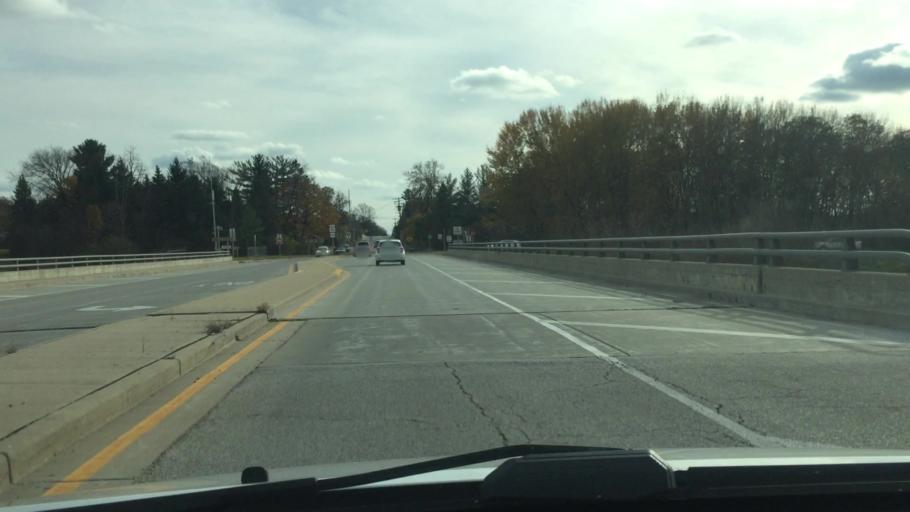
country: US
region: Wisconsin
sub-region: Waukesha County
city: Nashotah
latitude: 43.1022
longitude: -88.4030
